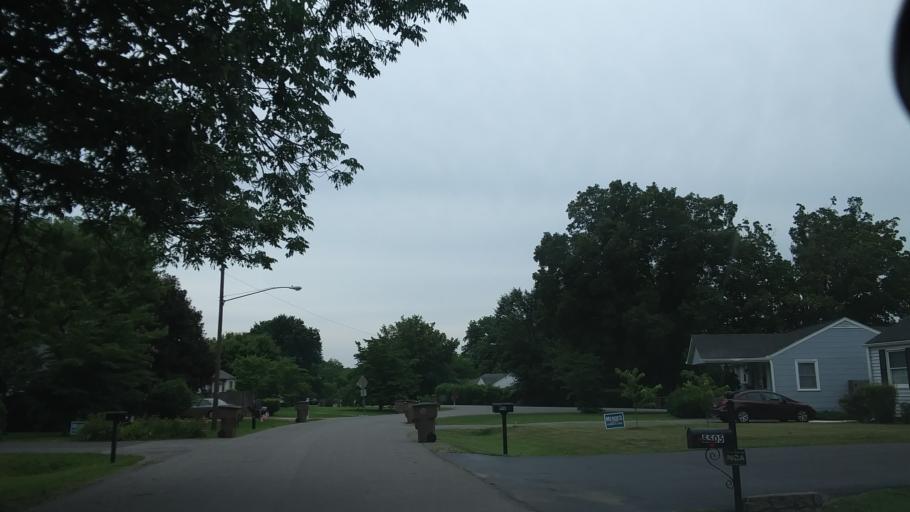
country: US
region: Tennessee
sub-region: Davidson County
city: Belle Meade
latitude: 36.1401
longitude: -86.8535
